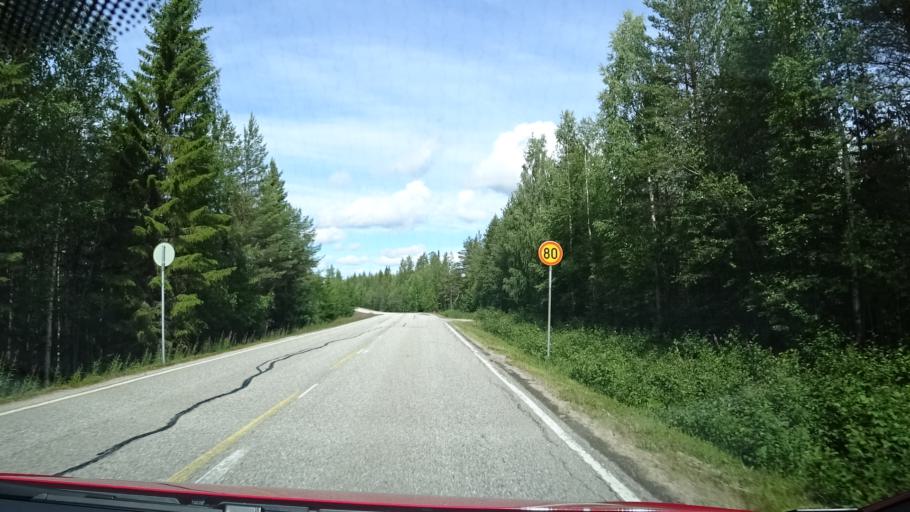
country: FI
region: Kainuu
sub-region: Kehys-Kainuu
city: Kuhmo
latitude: 64.4401
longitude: 29.8049
